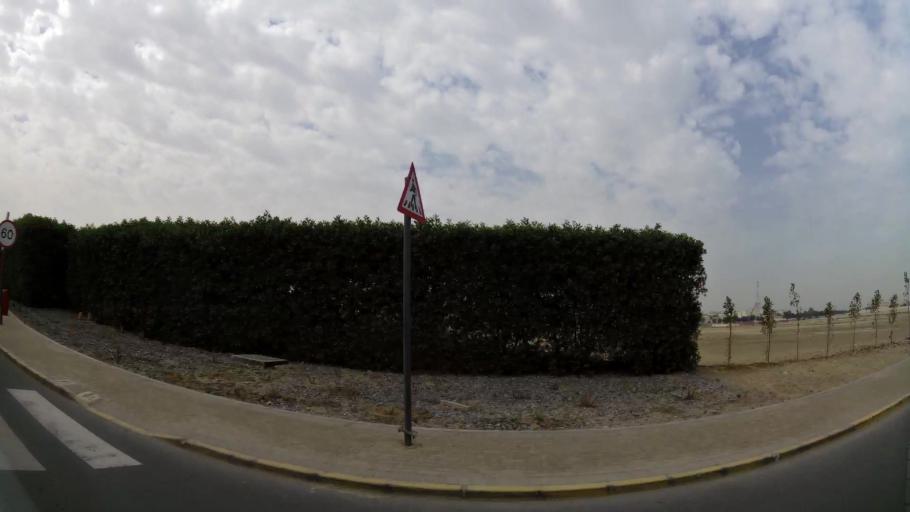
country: AE
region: Abu Dhabi
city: Abu Dhabi
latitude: 24.3116
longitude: 54.6178
